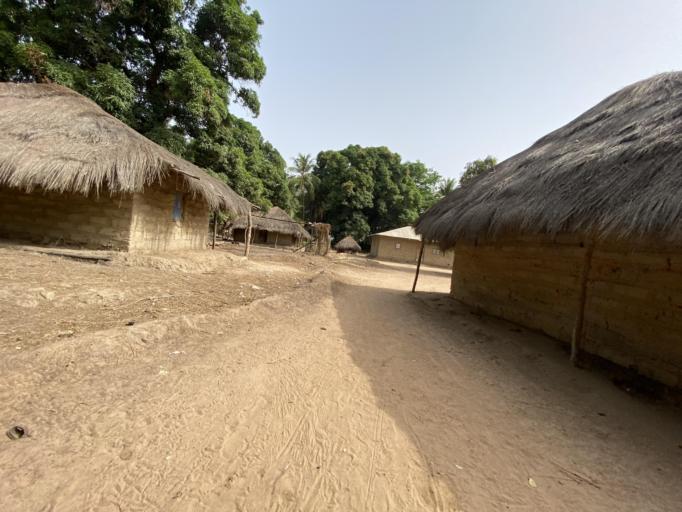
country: GW
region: Tombali
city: Quebo
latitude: 10.9475
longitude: -14.9634
